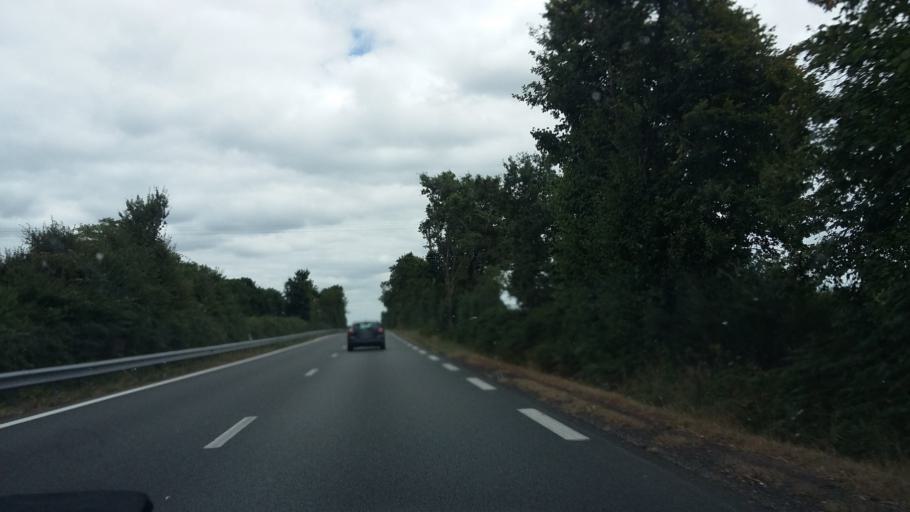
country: FR
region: Pays de la Loire
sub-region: Departement de la Vendee
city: Venansault
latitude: 46.7064
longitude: -1.5125
